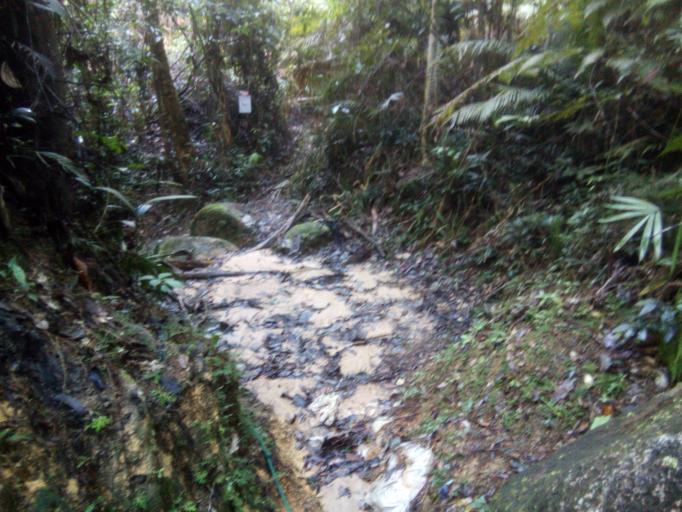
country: MY
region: Penang
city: Tanjung Tokong
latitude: 5.4174
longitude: 100.2595
